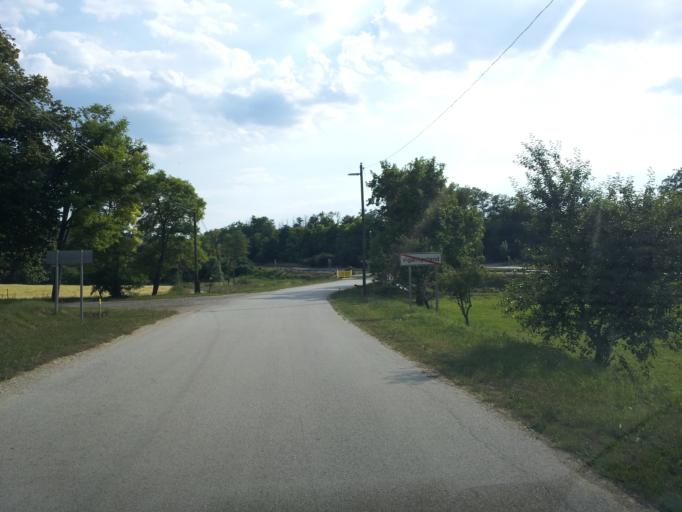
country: HU
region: Veszprem
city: Zanka
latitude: 46.9620
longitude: 17.6235
